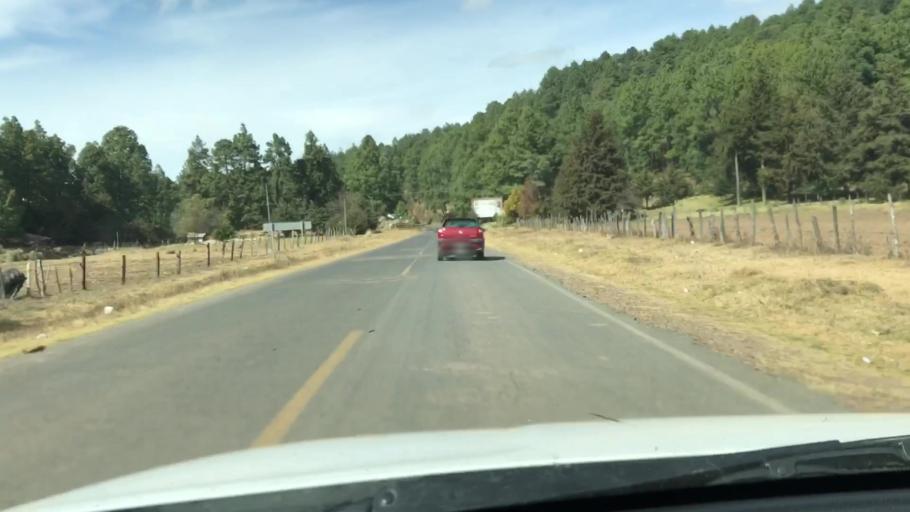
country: MX
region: Jalisco
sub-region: Amacueca
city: Tepec
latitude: 20.0407
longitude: -103.6913
